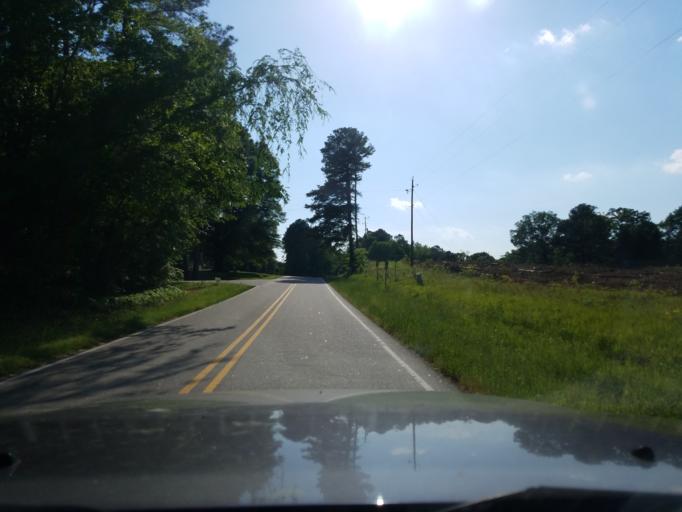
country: US
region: North Carolina
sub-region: Vance County
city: Henderson
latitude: 36.4081
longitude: -78.3836
